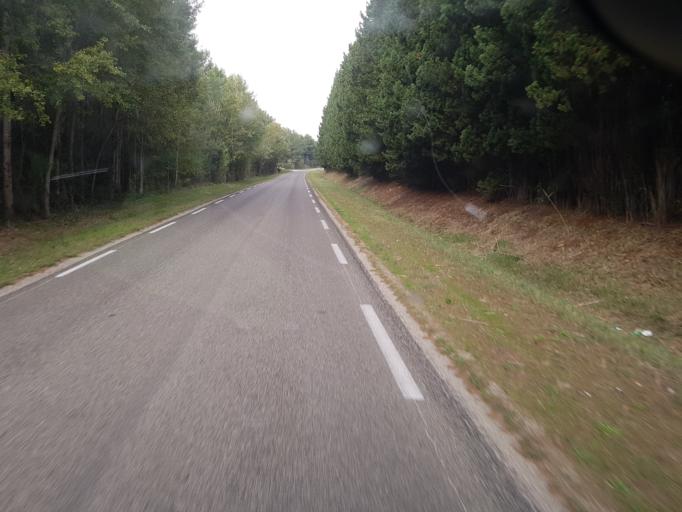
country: FR
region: Languedoc-Roussillon
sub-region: Departement du Gard
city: Aramon
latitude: 43.8886
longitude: 4.6979
